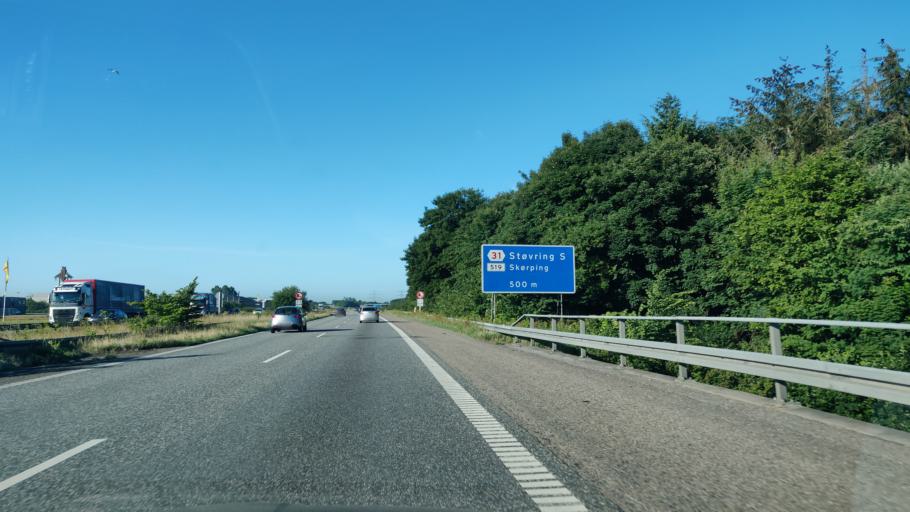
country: DK
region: North Denmark
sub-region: Rebild Kommune
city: Stovring
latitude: 56.8881
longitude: 9.8099
